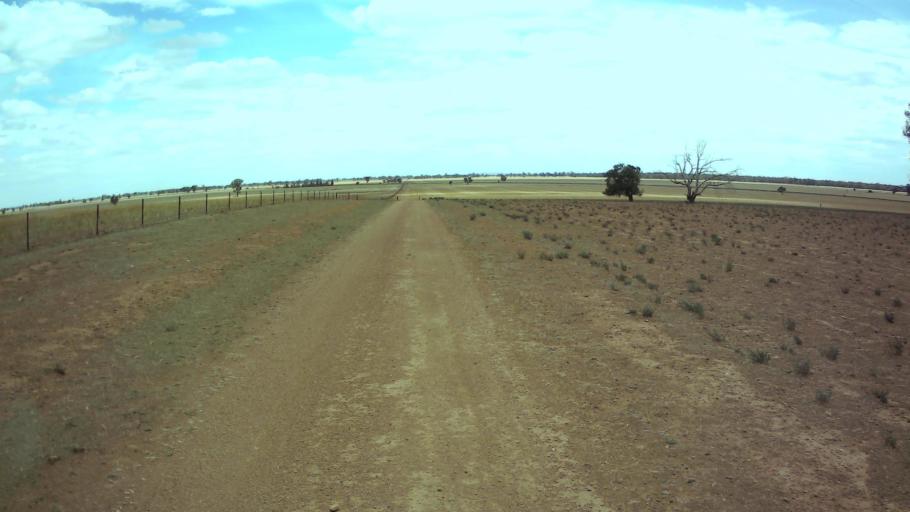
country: AU
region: New South Wales
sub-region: Weddin
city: Grenfell
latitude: -33.9018
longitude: 147.7393
